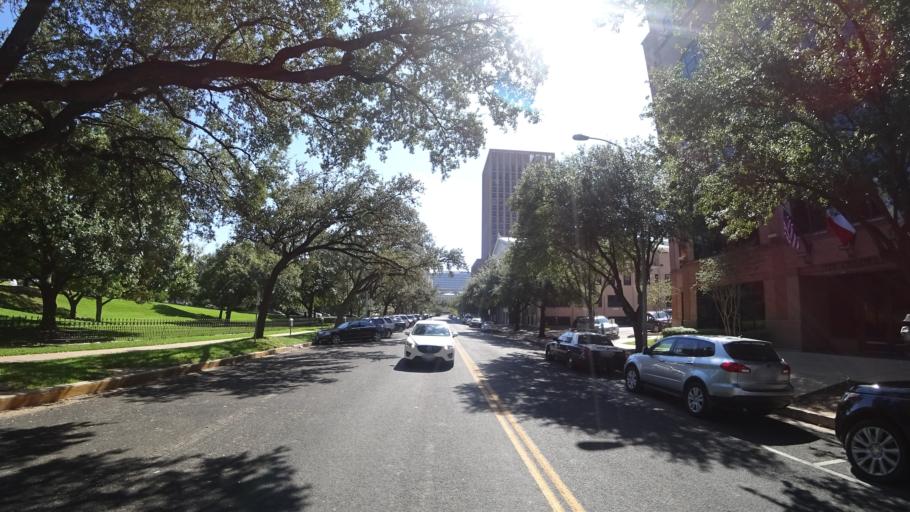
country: US
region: Texas
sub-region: Travis County
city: Austin
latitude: 30.2753
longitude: -97.7420
